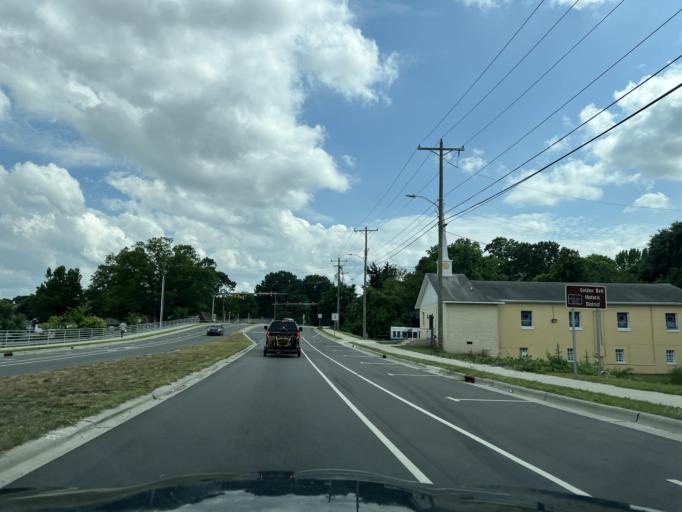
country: US
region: North Carolina
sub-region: Durham County
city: Durham
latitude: 35.9917
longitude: -78.8862
